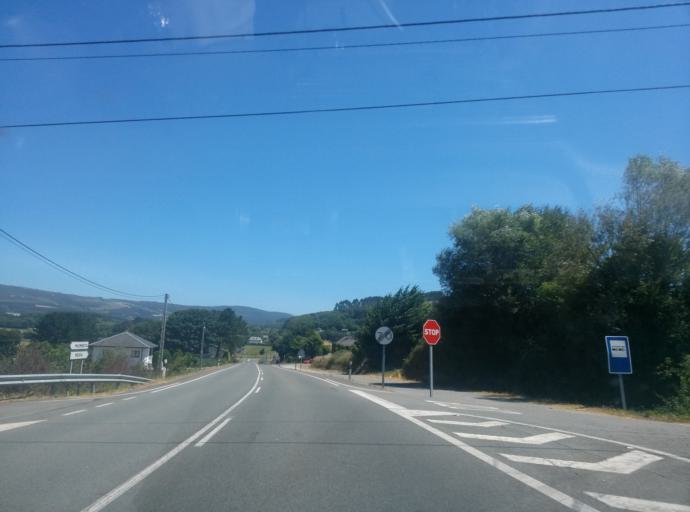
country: ES
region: Galicia
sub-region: Provincia de Lugo
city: Meira
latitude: 43.2237
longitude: -7.3254
